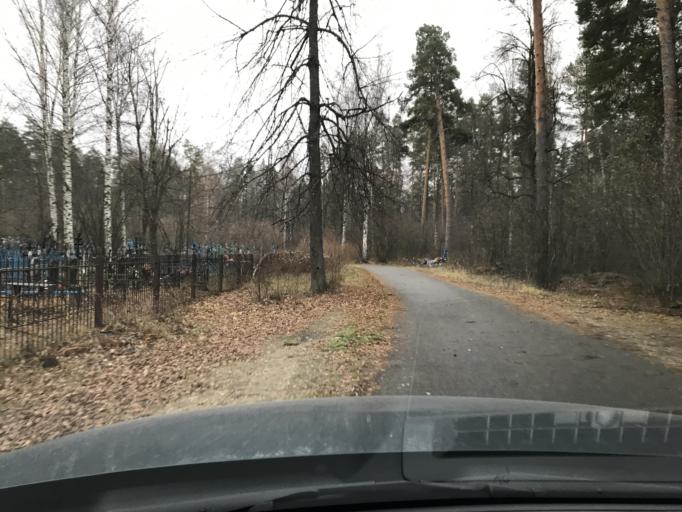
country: RU
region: Mordoviya
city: Shiringushi
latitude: 53.8515
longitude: 42.7892
